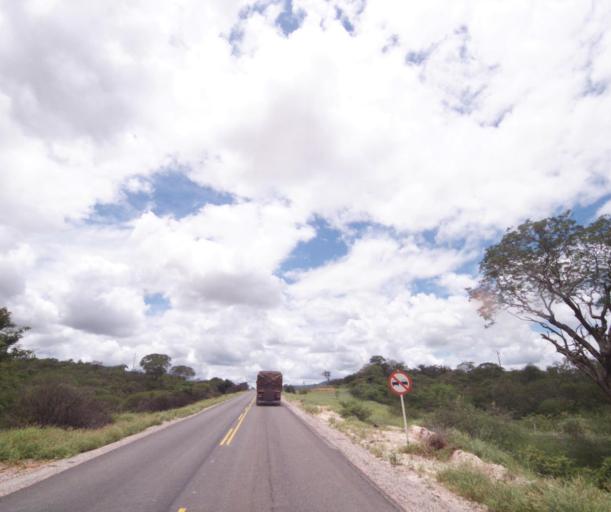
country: BR
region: Bahia
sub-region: Brumado
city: Brumado
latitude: -14.1510
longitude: -41.5048
